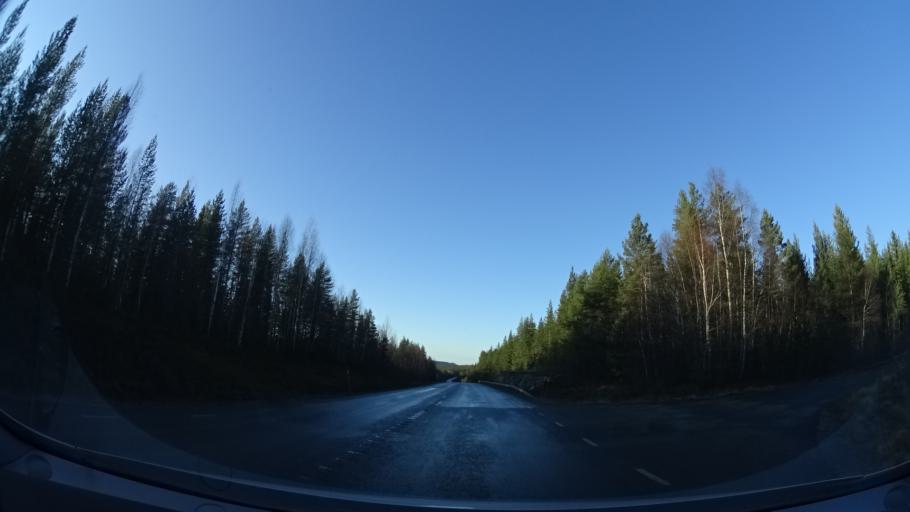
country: SE
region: Vaesterbotten
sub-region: Skelleftea Kommun
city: Langsele
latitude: 64.8913
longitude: 20.1762
